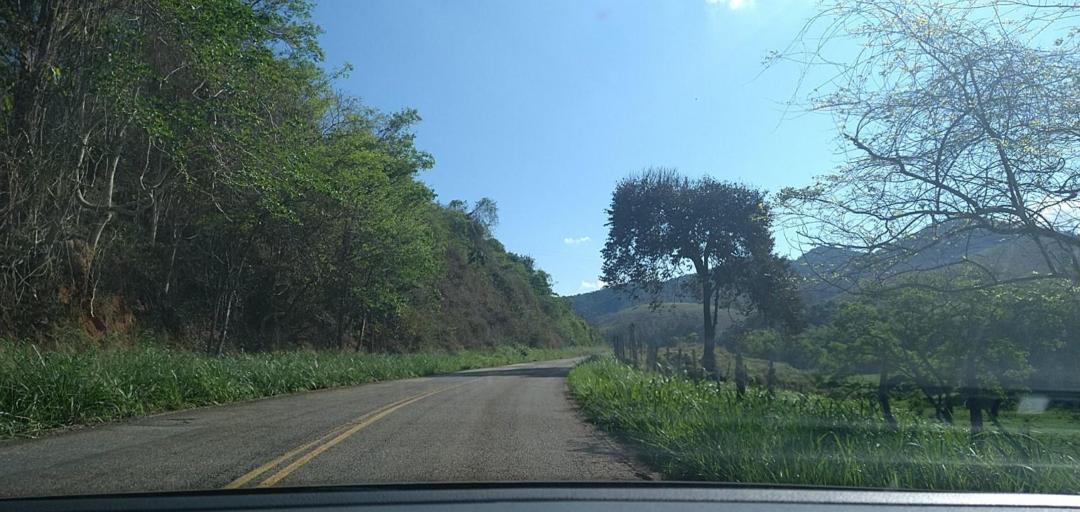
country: BR
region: Minas Gerais
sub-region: Alvinopolis
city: Alvinopolis
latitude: -20.1834
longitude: -42.9331
